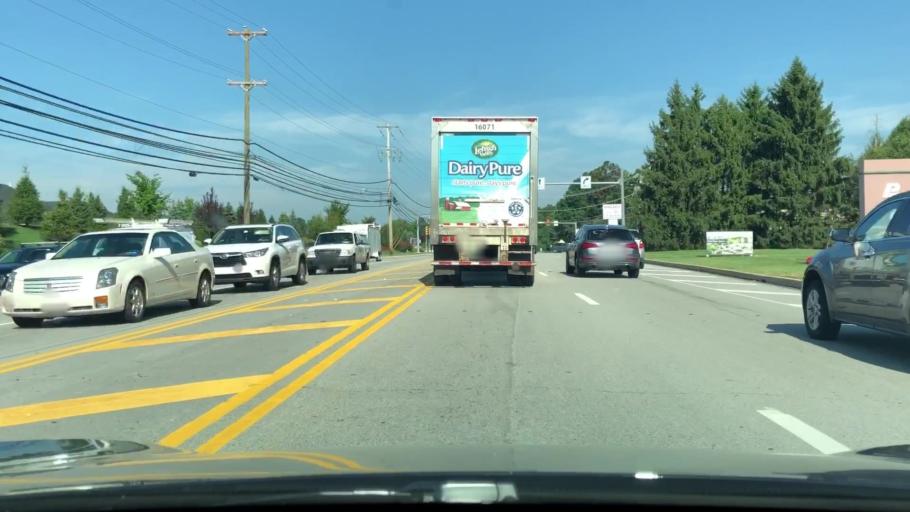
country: US
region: Pennsylvania
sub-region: Montgomery County
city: Dresher
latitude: 40.1610
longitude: -75.1498
